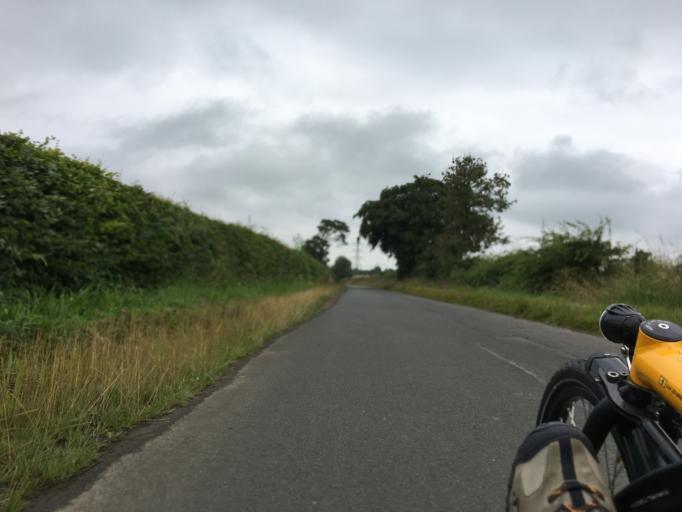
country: GB
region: Scotland
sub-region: West Lothian
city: West Calder
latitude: 55.8475
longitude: -3.5142
